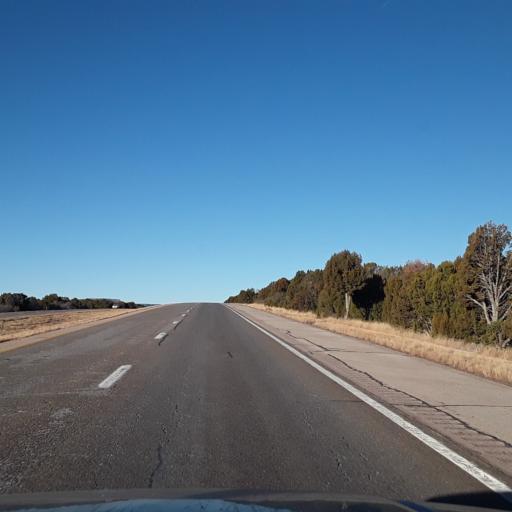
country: US
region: New Mexico
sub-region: San Miguel County
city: Las Vegas
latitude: 35.3926
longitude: -105.3522
